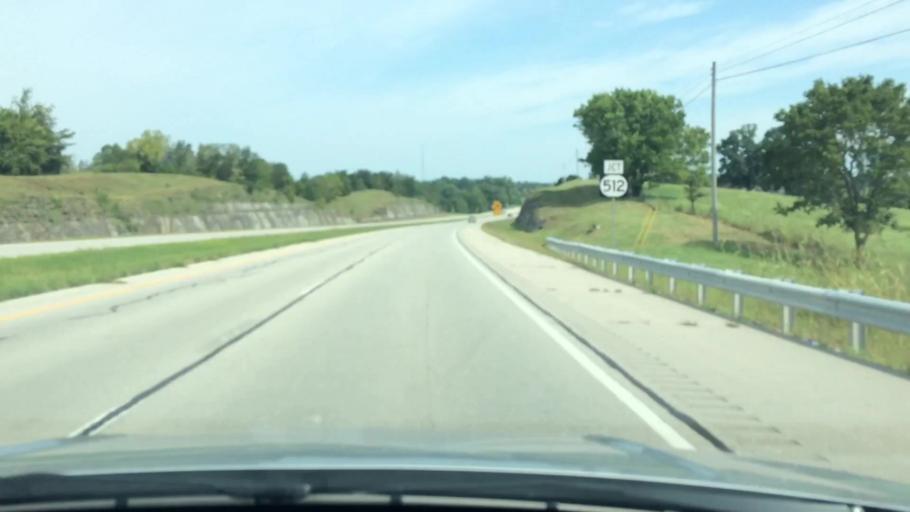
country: US
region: Kentucky
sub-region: Anderson County
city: Lawrenceburg
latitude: 38.0944
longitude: -84.9195
